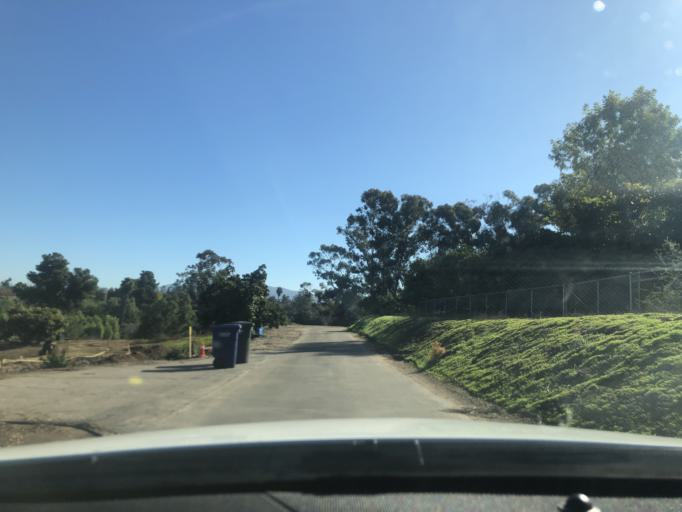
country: US
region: California
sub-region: San Diego County
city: Casa de Oro-Mount Helix
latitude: 32.7740
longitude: -116.9435
